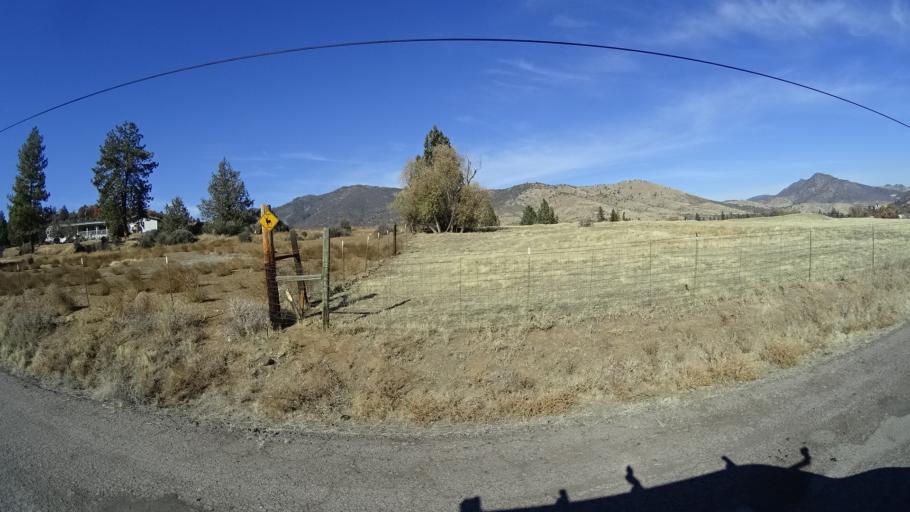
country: US
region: California
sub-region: Siskiyou County
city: Yreka
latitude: 41.7600
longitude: -122.6280
